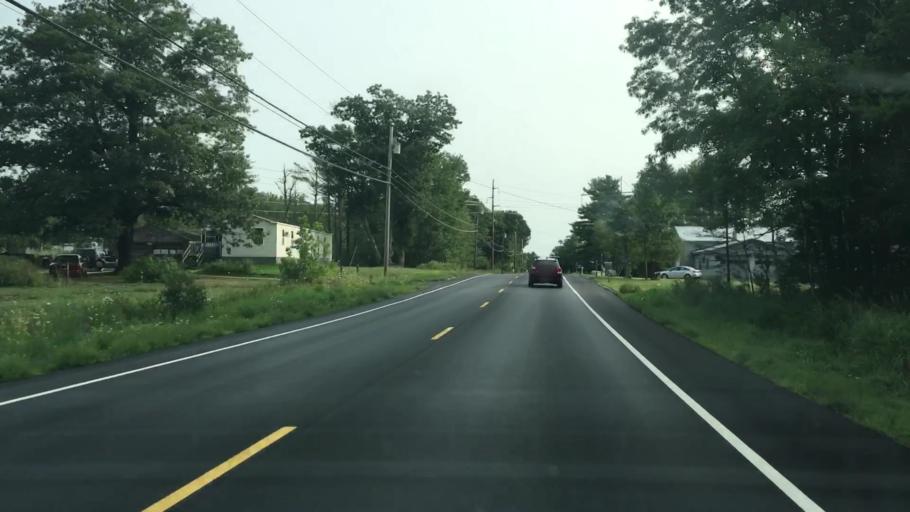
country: US
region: Maine
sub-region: Kennebec County
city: Chelsea
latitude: 44.2624
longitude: -69.7044
